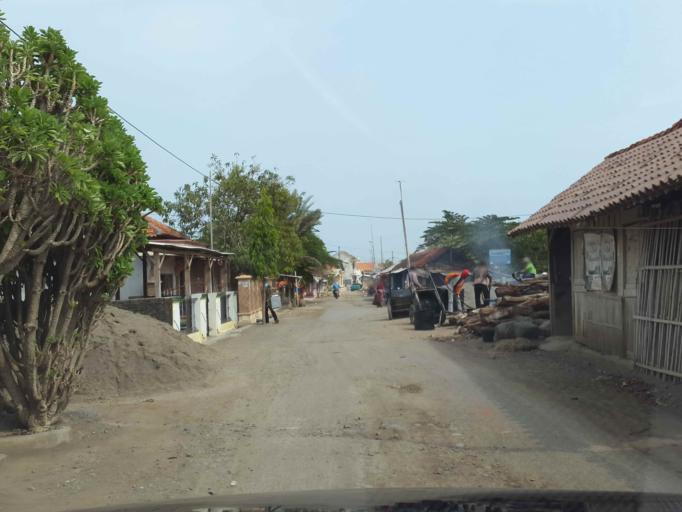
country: ID
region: Central Java
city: Bulakamba
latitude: -6.8540
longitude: 108.8842
